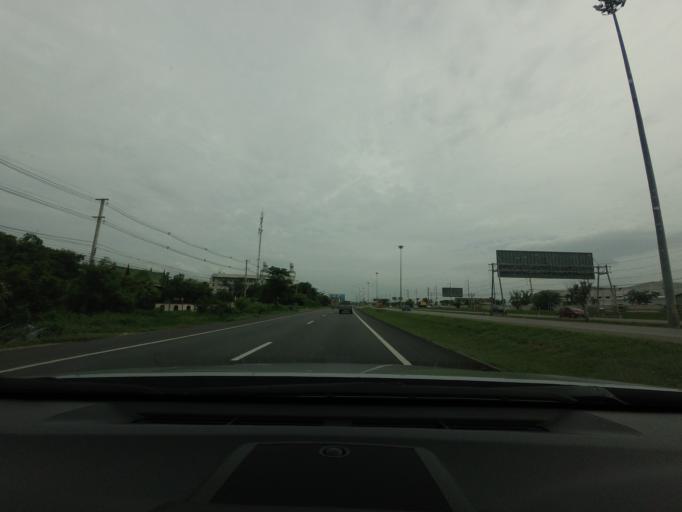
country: TH
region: Ratchaburi
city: Pak Tho
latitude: 13.3367
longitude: 99.8308
